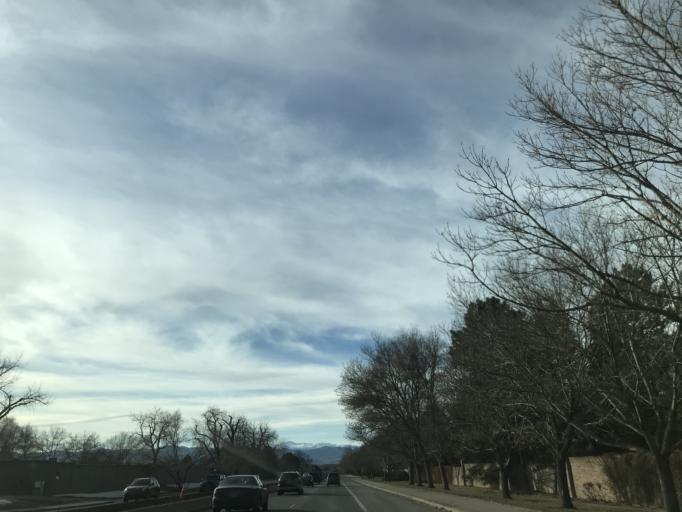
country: US
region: Colorado
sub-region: Arapahoe County
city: Greenwood Village
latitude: 39.6243
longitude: -104.9520
